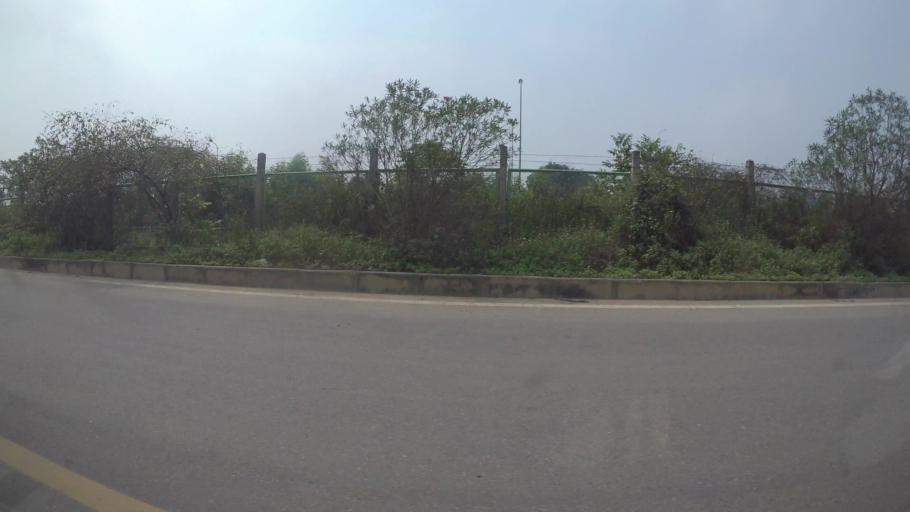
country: VN
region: Ha Noi
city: Lien Quan
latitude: 20.9909
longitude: 105.5504
